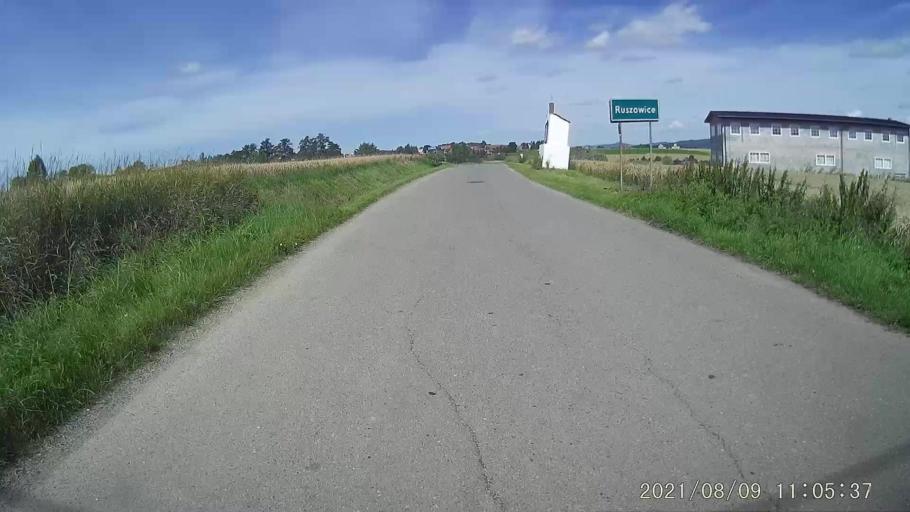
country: PL
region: Lower Silesian Voivodeship
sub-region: Powiat klodzki
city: Bozkow
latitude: 50.4595
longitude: 16.5806
